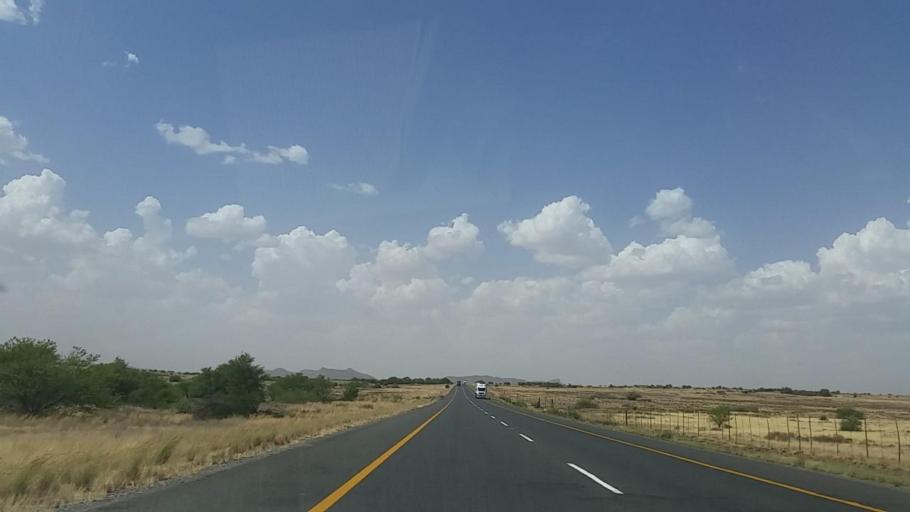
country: ZA
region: Northern Cape
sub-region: Pixley ka Seme District Municipality
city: Colesberg
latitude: -30.5763
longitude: 25.4410
